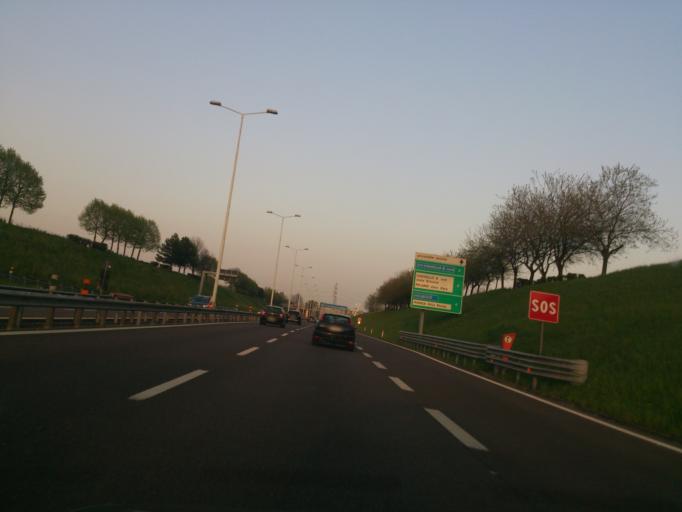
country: IT
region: Lombardy
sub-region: Provincia di Monza e Brianza
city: Nova Milanese
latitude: 45.5766
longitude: 9.2095
